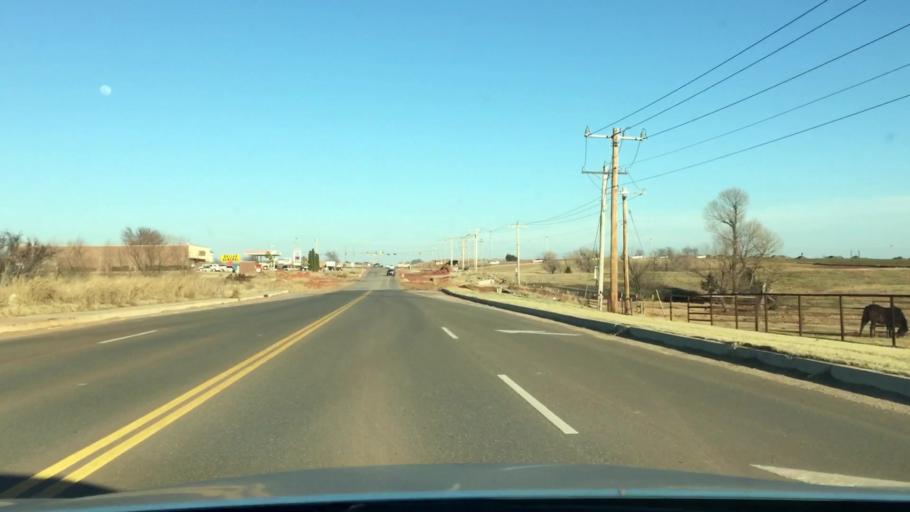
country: US
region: Oklahoma
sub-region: Oklahoma County
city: The Village
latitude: 35.6531
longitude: -97.5895
